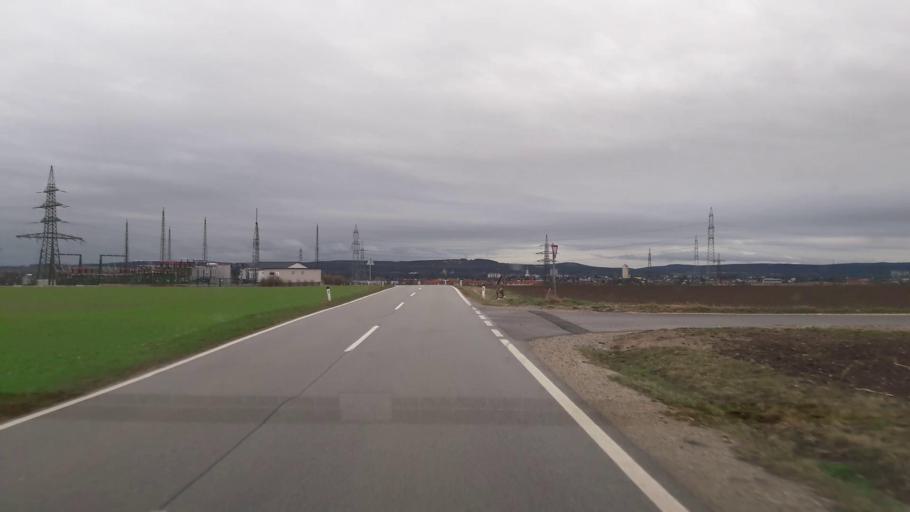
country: AT
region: Burgenland
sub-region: Politischer Bezirk Neusiedl am See
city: Bruckneudorf
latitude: 48.0500
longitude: 16.7847
